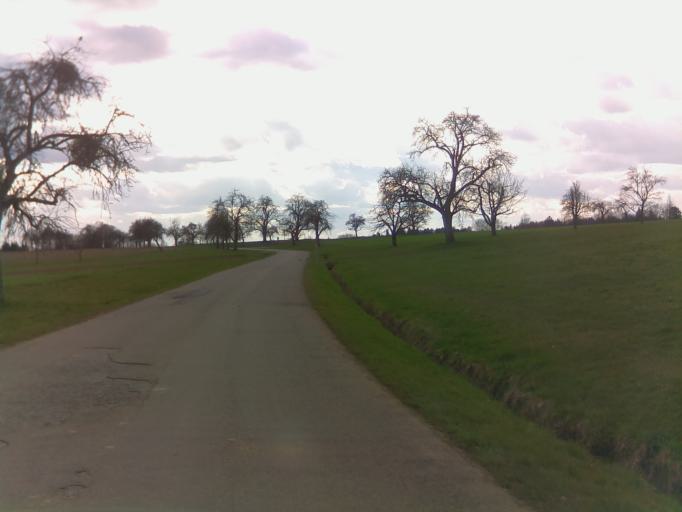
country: DE
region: Baden-Wuerttemberg
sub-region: Regierungsbezirk Stuttgart
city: Lorch
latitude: 48.8366
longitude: 9.6735
